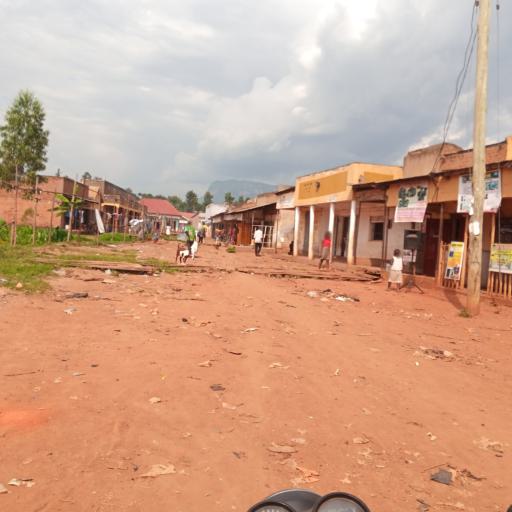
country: UG
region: Eastern Region
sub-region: Mbale District
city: Mbale
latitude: 1.0937
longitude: 34.1771
